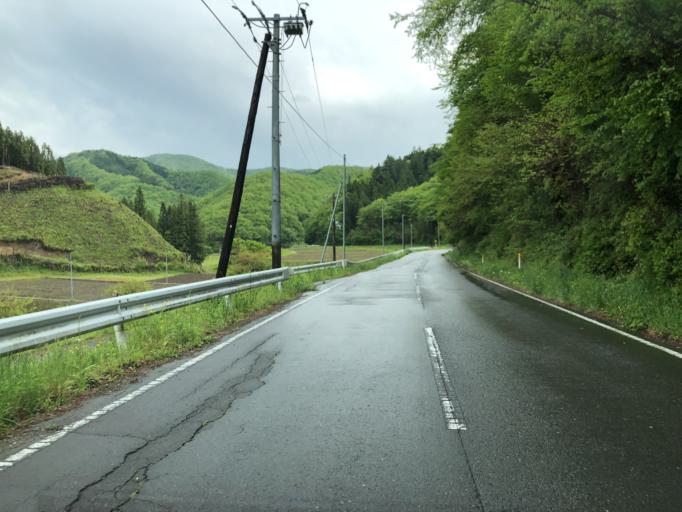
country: JP
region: Fukushima
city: Ishikawa
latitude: 36.9961
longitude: 140.6138
